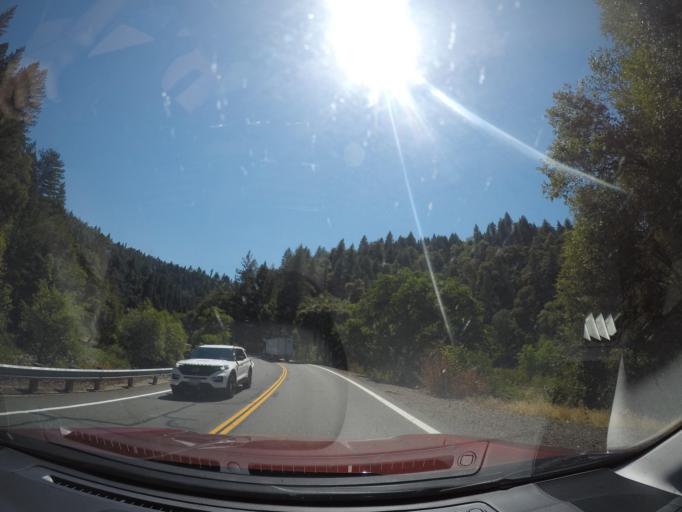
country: US
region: California
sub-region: Shasta County
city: Bella Vista
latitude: 40.7491
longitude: -122.0534
